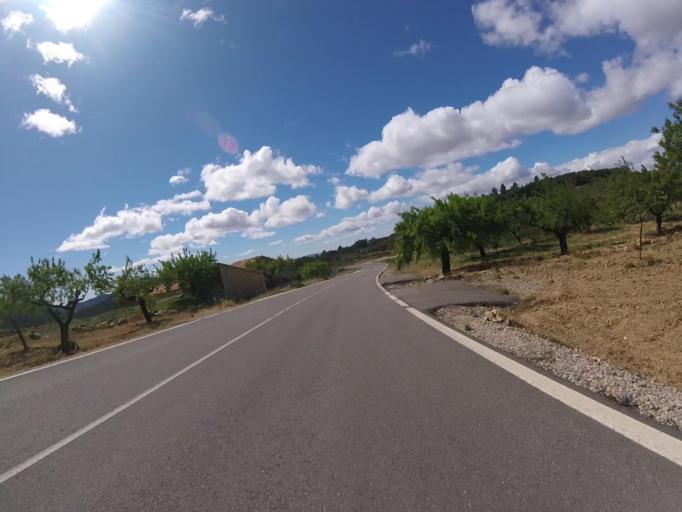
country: ES
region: Valencia
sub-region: Provincia de Castello
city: Culla
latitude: 40.2986
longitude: -0.1191
